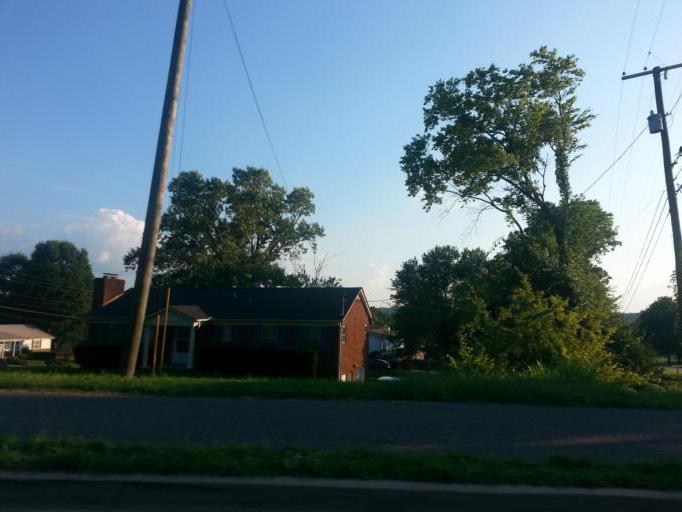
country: US
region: Tennessee
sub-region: Knox County
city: Knoxville
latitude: 35.9882
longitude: -83.9971
